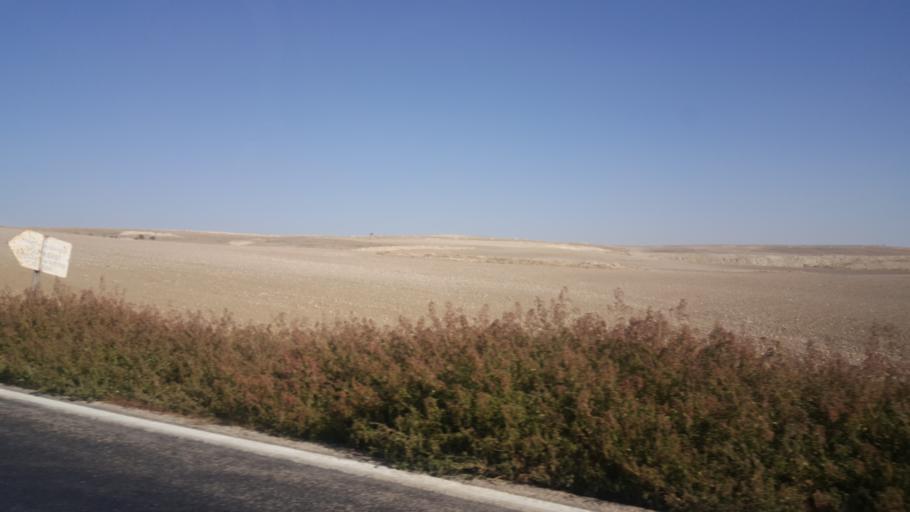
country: TR
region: Konya
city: Celtik
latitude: 39.0738
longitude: 32.0949
